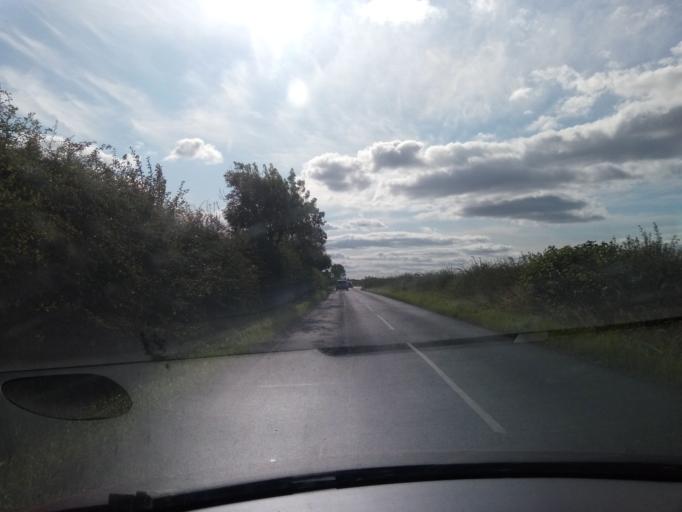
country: GB
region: Scotland
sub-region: The Scottish Borders
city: Allanton
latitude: 55.7410
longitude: -2.1849
